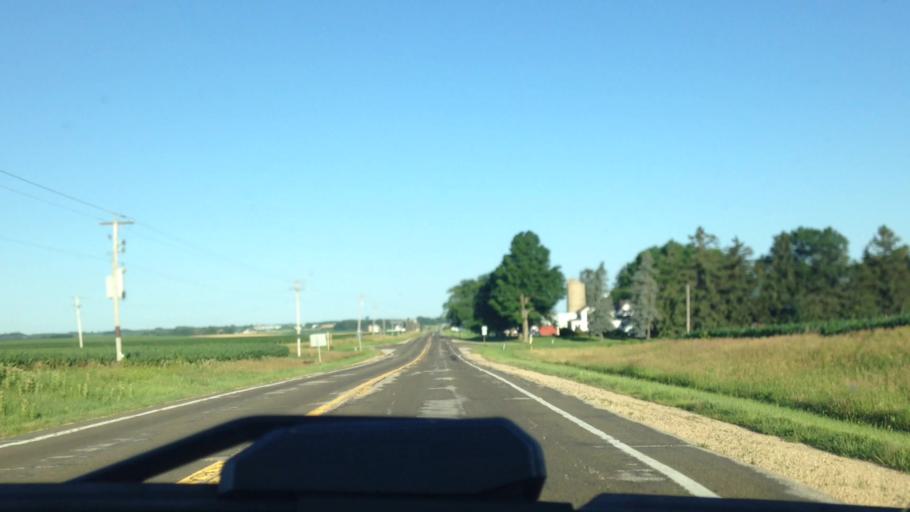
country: US
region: Wisconsin
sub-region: Columbia County
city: Poynette
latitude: 43.3378
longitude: -89.4206
